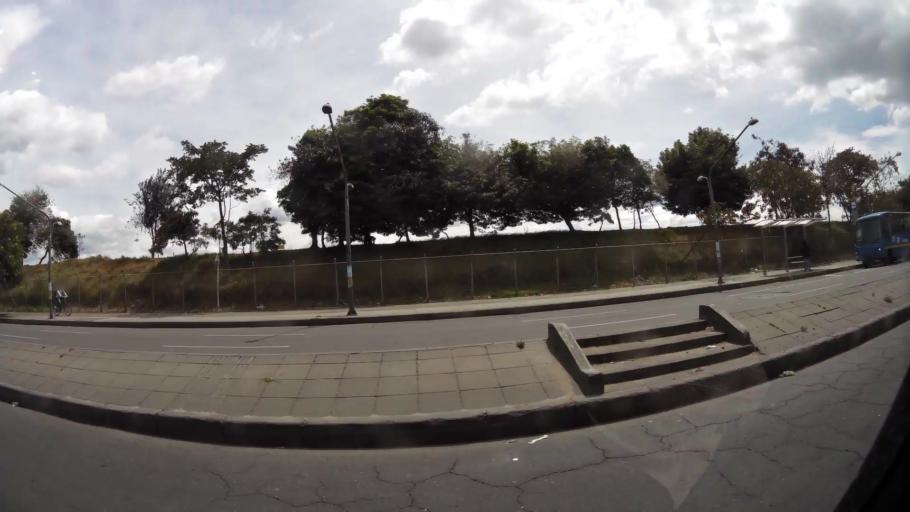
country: CO
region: Cundinamarca
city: Funza
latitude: 4.7015
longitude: -74.1333
